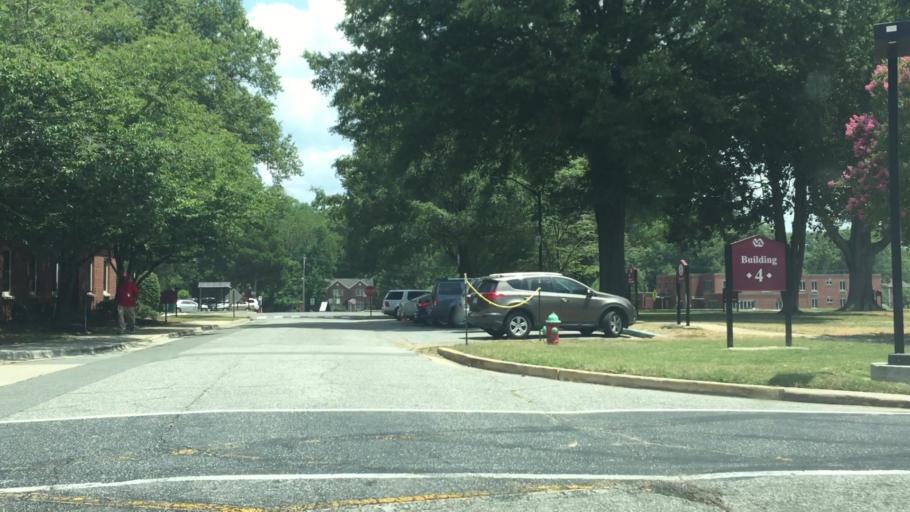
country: US
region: North Carolina
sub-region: Rowan County
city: Salisbury
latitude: 35.6836
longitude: -80.4883
